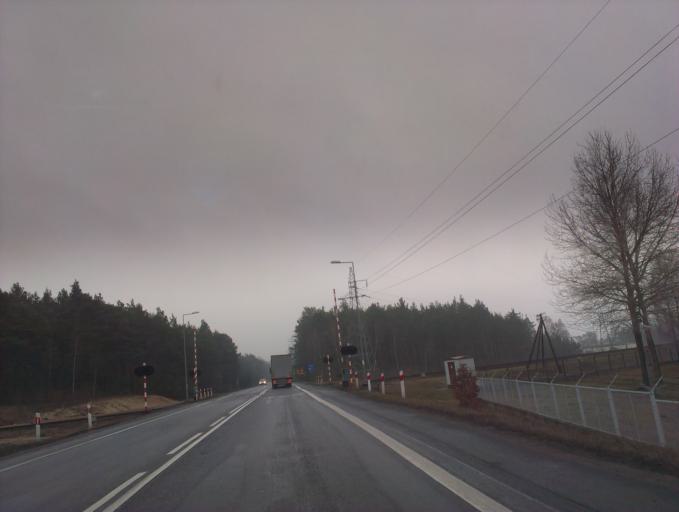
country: PL
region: Greater Poland Voivodeship
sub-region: Powiat pilski
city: Pila
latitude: 53.1685
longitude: 16.7814
